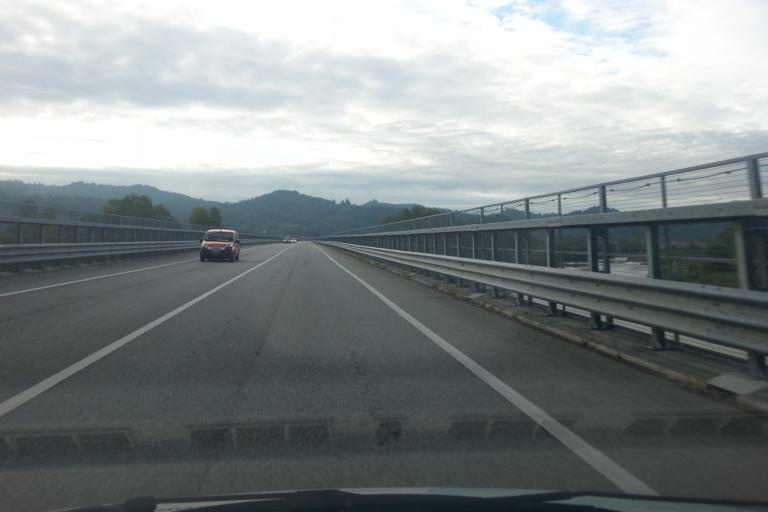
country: IT
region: Piedmont
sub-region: Provincia di Torino
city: Piana San Raffaele
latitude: 45.1553
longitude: 7.8320
